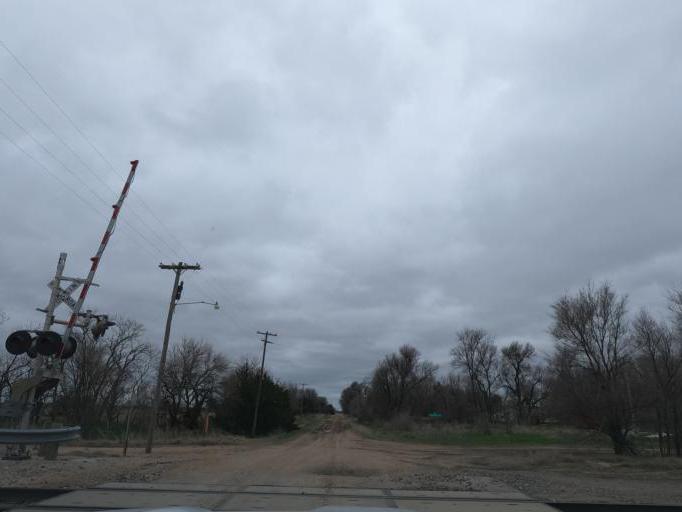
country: US
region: Kansas
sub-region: Rice County
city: Sterling
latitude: 37.9742
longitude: -98.3072
